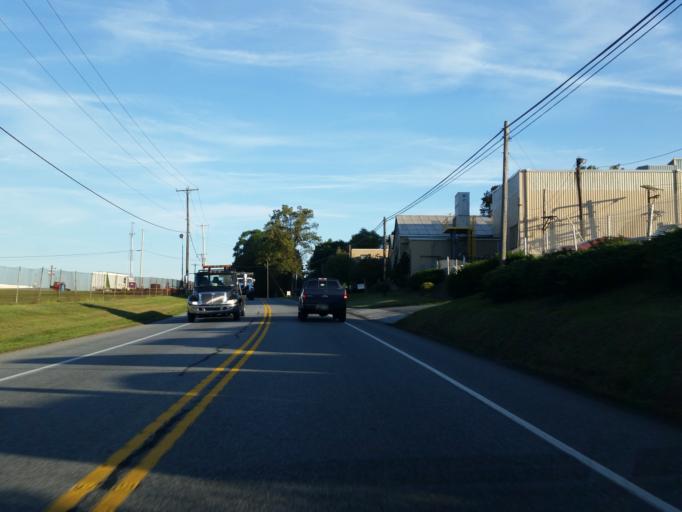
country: US
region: Pennsylvania
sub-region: Lancaster County
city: Quarryville
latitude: 39.8811
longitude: -76.2312
